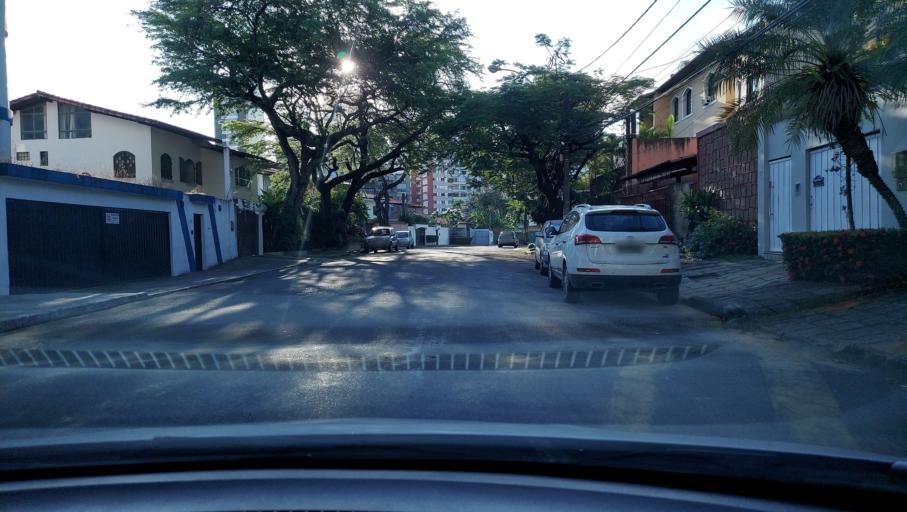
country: BR
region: Bahia
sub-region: Salvador
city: Salvador
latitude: -12.9875
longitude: -38.4559
